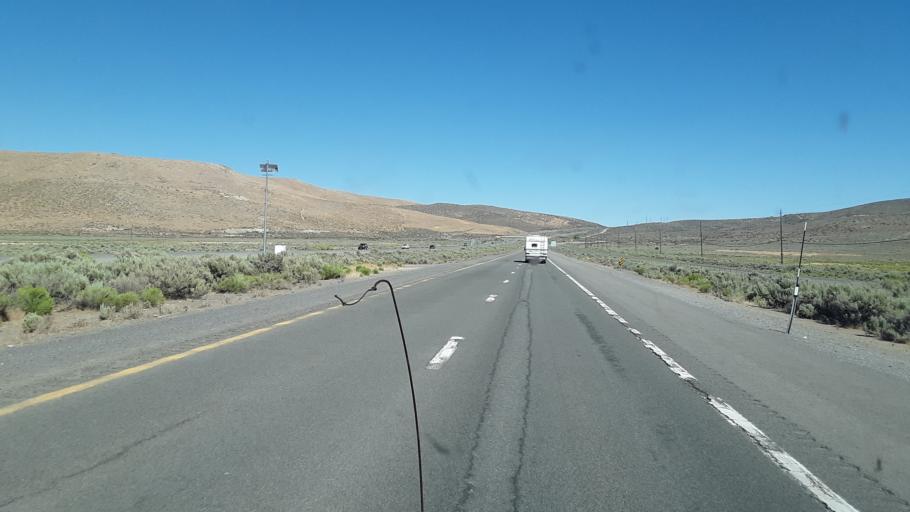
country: US
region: Nevada
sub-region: Washoe County
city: Cold Springs
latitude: 39.6485
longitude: -119.9723
